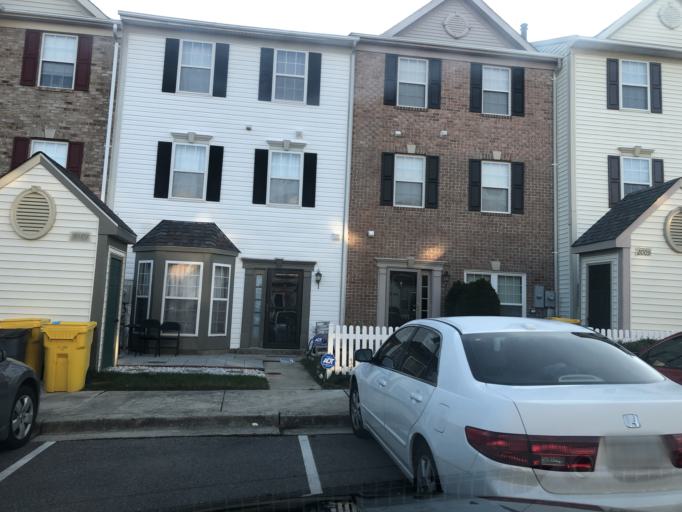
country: US
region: Maryland
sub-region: Anne Arundel County
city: Odenton
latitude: 39.1007
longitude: -76.7123
